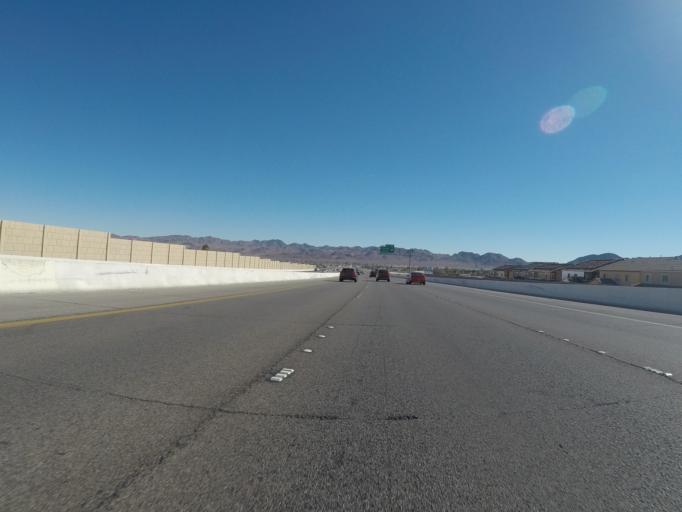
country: US
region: Nevada
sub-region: Clark County
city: Henderson
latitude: 35.9999
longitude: -114.9714
